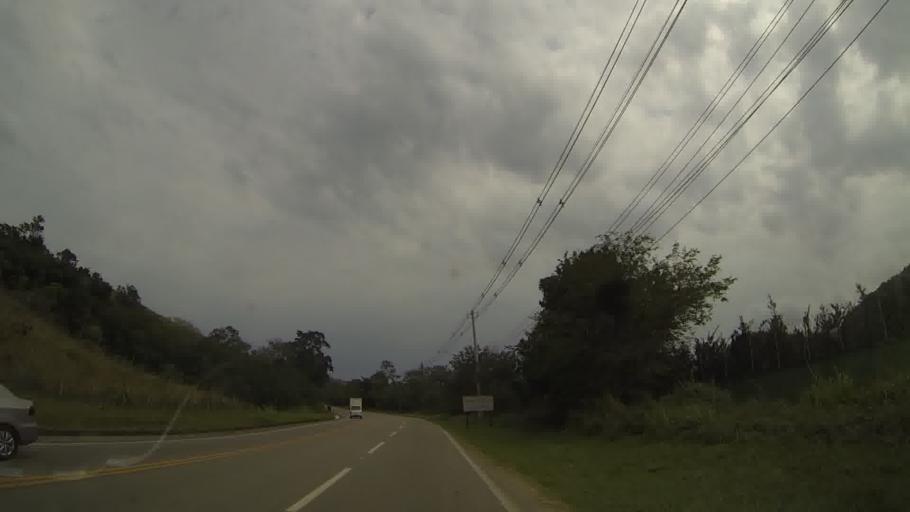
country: BR
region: Sao Paulo
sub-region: Sao Sebastiao
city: Sao Sebastiao
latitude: -23.7996
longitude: -45.5439
